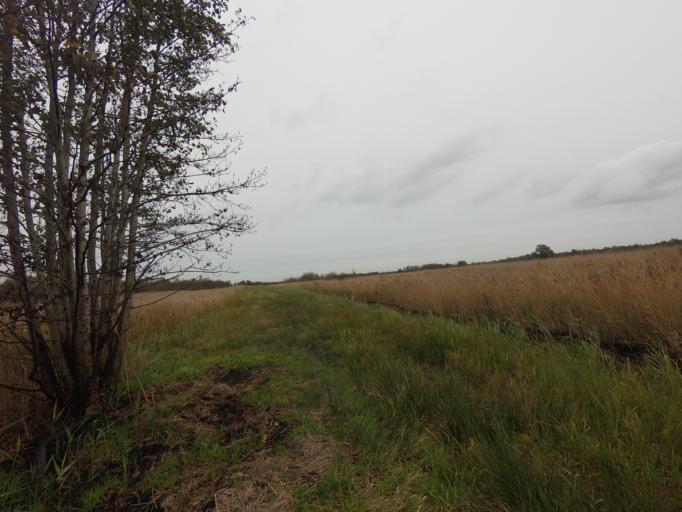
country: NL
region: Overijssel
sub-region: Gemeente Steenwijkerland
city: Oldemarkt
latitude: 52.7753
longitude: 5.9620
